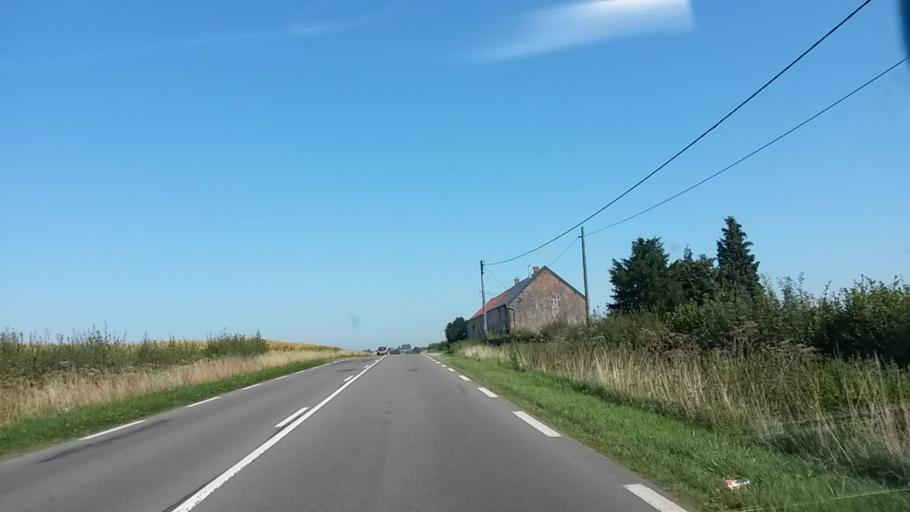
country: FR
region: Nord-Pas-de-Calais
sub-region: Departement du Nord
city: Hautmont
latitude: 50.2005
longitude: 3.9505
